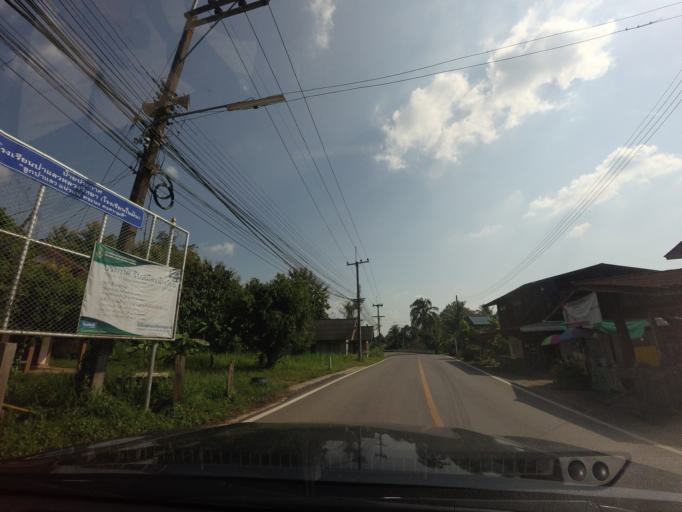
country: TH
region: Nan
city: Santi Suk
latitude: 18.9380
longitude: 100.9262
